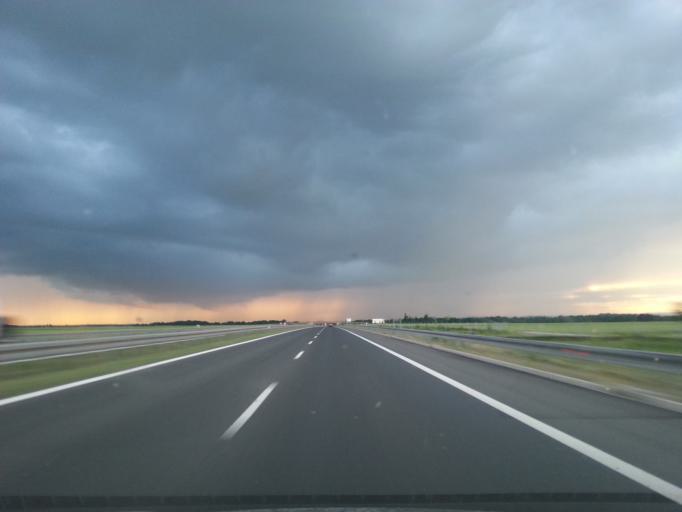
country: PL
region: Lower Silesian Voivodeship
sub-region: Powiat olesnicki
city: Dobroszyce
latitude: 51.2254
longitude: 17.2851
